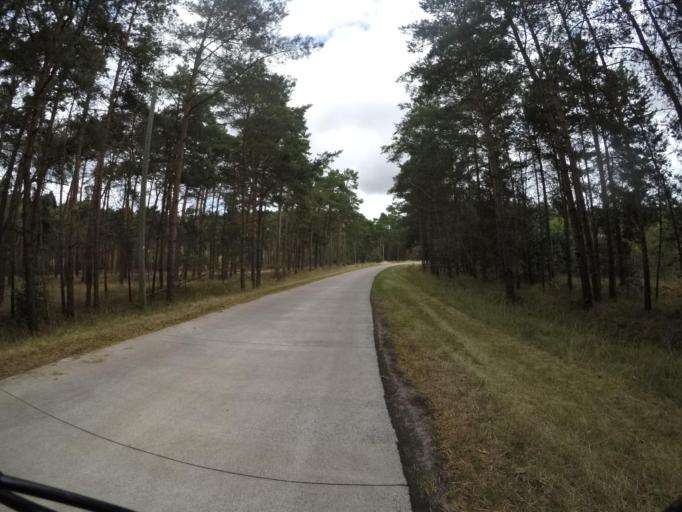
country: DE
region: Lower Saxony
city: Damnatz
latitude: 53.1857
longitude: 11.1213
